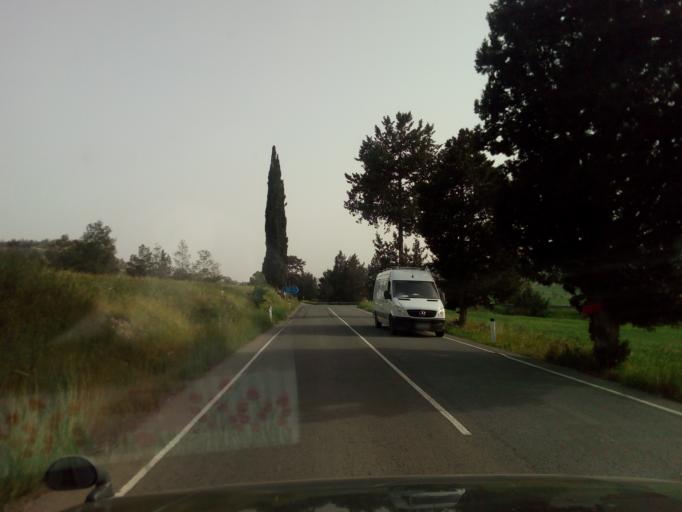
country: CY
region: Lefkosia
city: Lympia
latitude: 35.0030
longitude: 33.4992
